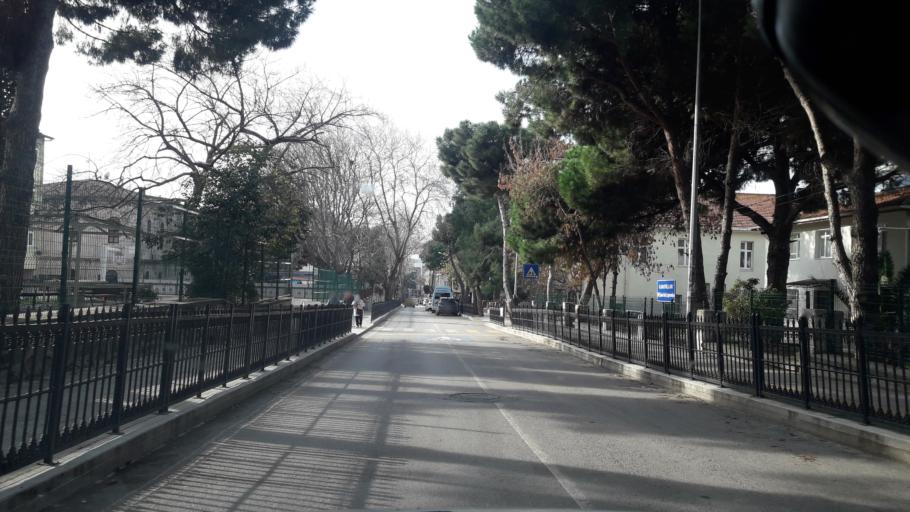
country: TR
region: Sinop
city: Sinop
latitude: 42.0288
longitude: 35.1544
